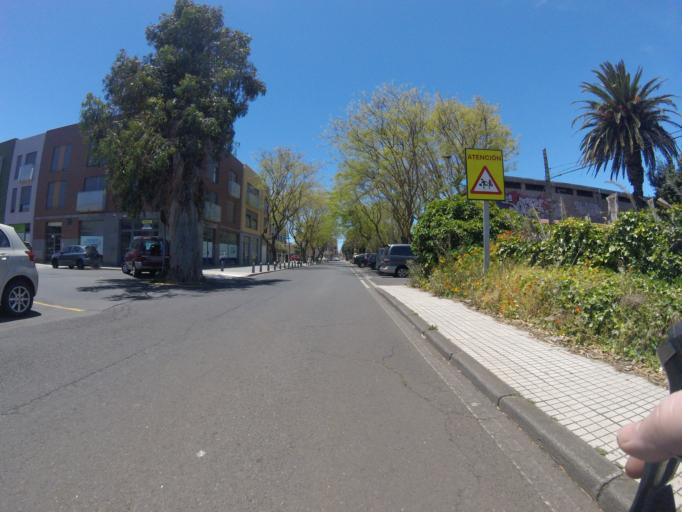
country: ES
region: Canary Islands
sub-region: Provincia de Santa Cruz de Tenerife
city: La Laguna
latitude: 28.4941
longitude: -16.3152
